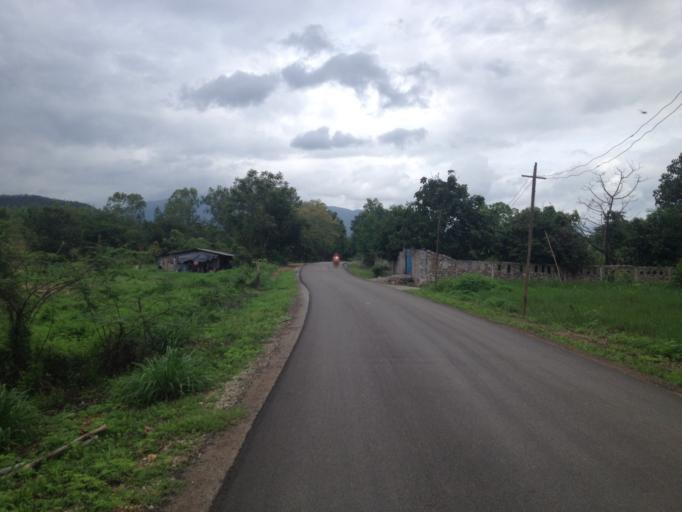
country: TH
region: Chiang Mai
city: Hang Dong
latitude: 18.7116
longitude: 98.9041
